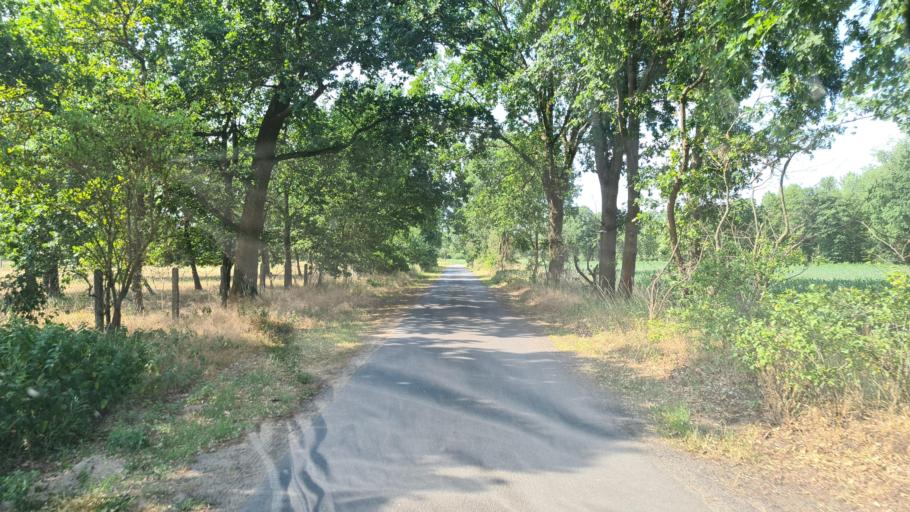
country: DE
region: Brandenburg
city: Wollin
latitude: 52.3271
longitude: 12.5433
